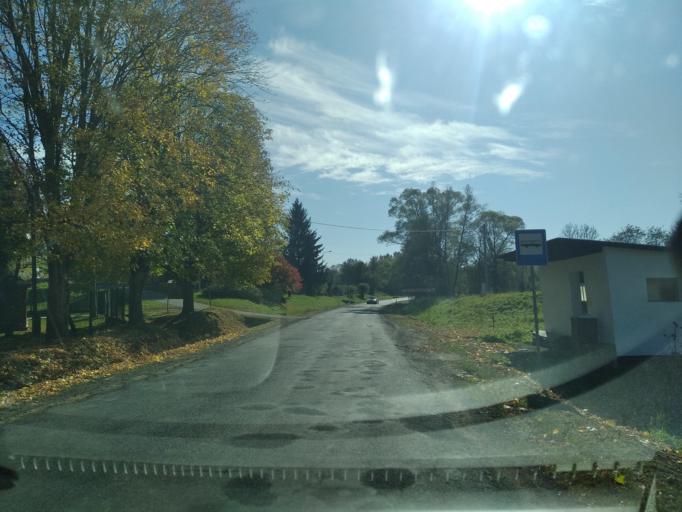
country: PL
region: Subcarpathian Voivodeship
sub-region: Powiat sanocki
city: Bukowsko
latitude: 49.4110
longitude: 21.9790
